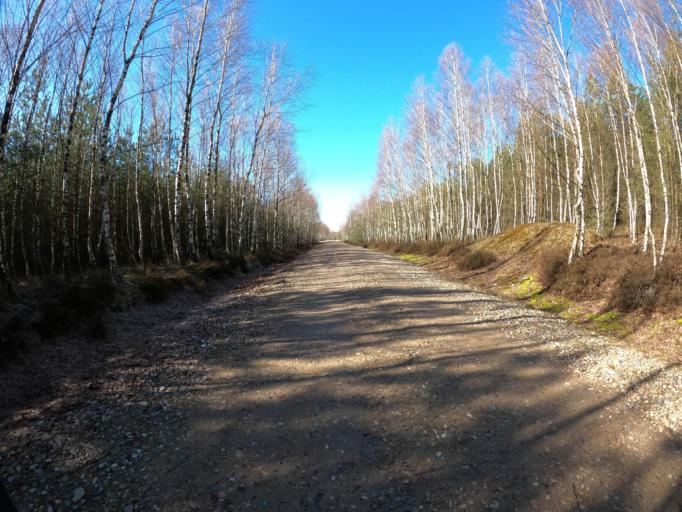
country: PL
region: Greater Poland Voivodeship
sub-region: Powiat zlotowski
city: Sypniewo
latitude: 53.5345
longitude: 16.6043
